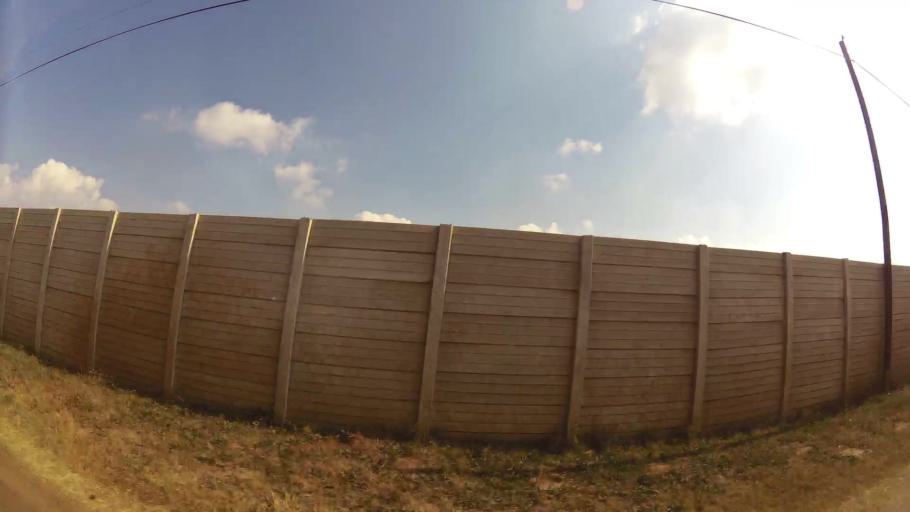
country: ZA
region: Mpumalanga
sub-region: Nkangala District Municipality
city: Delmas
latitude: -26.1885
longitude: 28.5400
